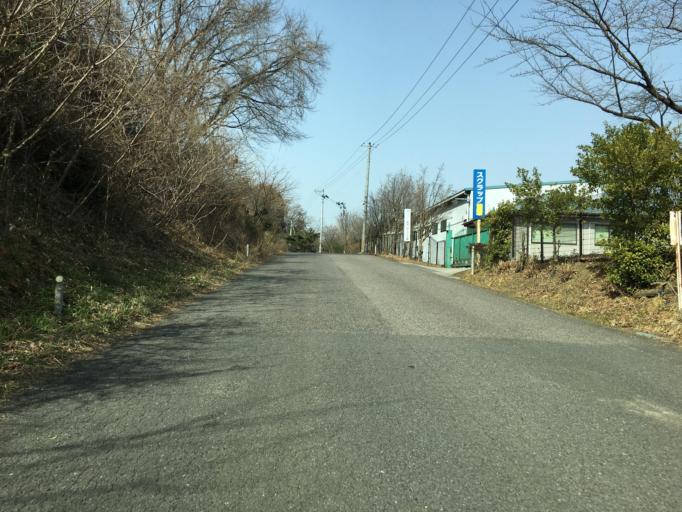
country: JP
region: Fukushima
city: Motomiya
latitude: 37.5320
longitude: 140.4112
